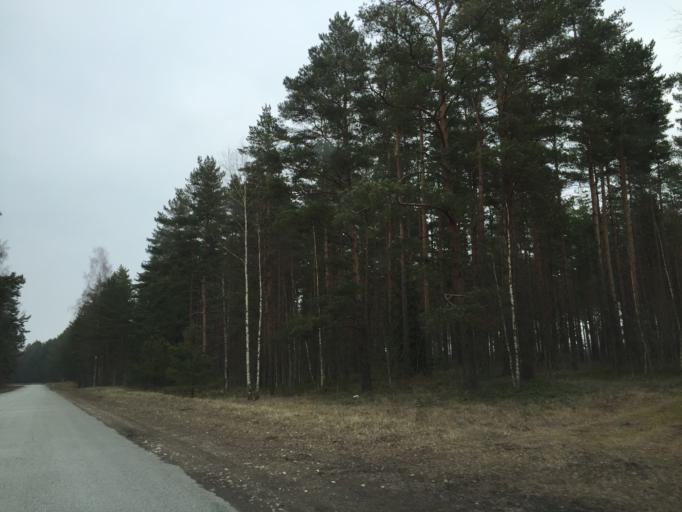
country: LV
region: Salacgrivas
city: Ainazi
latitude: 58.0241
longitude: 24.4557
